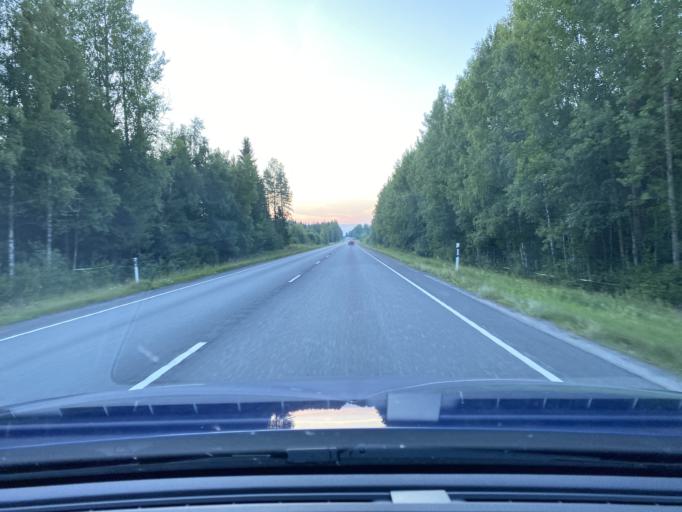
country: FI
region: Pirkanmaa
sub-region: Luoteis-Pirkanmaa
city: Ikaalinen
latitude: 61.8263
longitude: 22.9457
